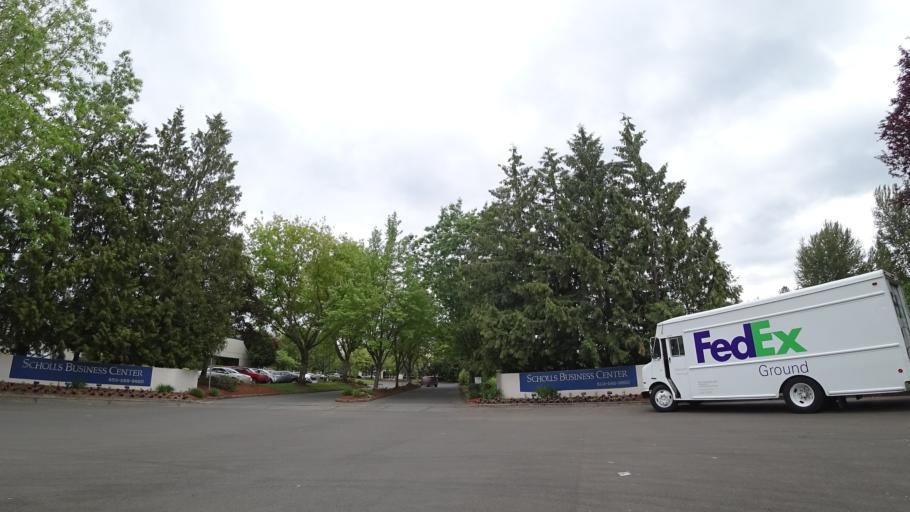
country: US
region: Oregon
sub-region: Washington County
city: Tigard
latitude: 45.4452
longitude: -122.7872
